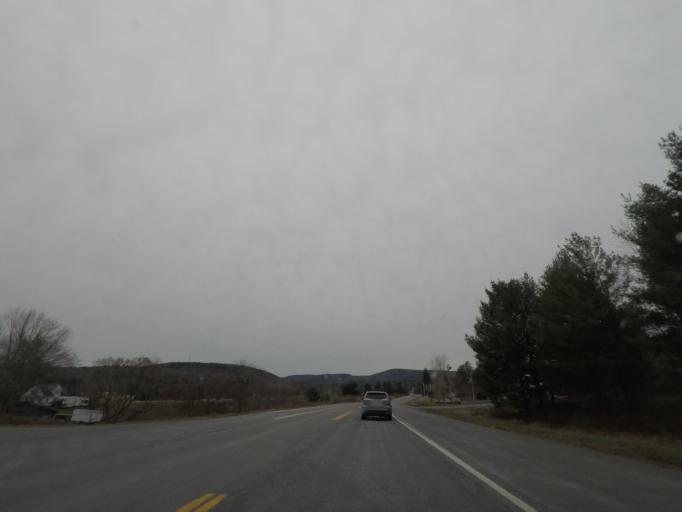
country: US
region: Massachusetts
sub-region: Berkshire County
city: Lanesborough
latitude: 42.5455
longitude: -73.3574
